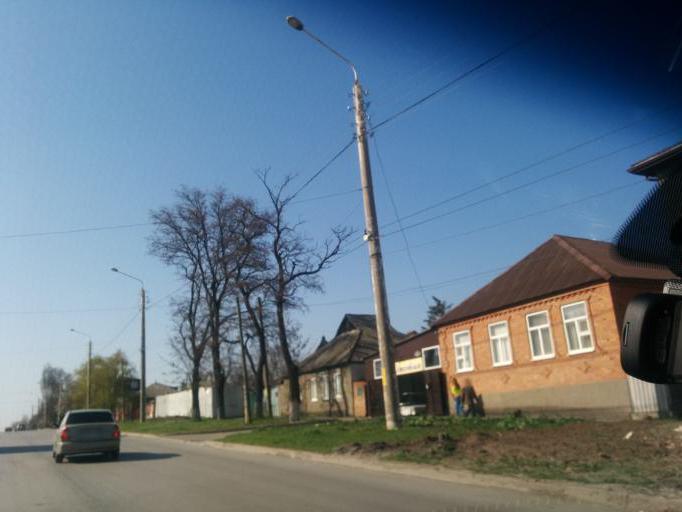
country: RU
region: Rostov
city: Shakhty
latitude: 47.6994
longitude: 40.2057
